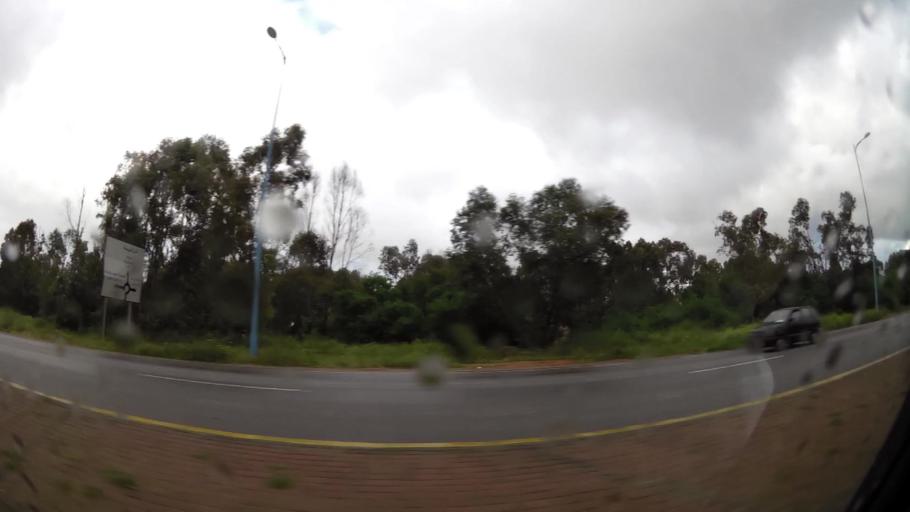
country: MA
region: Grand Casablanca
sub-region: Mohammedia
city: Mohammedia
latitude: 33.6771
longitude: -7.4107
